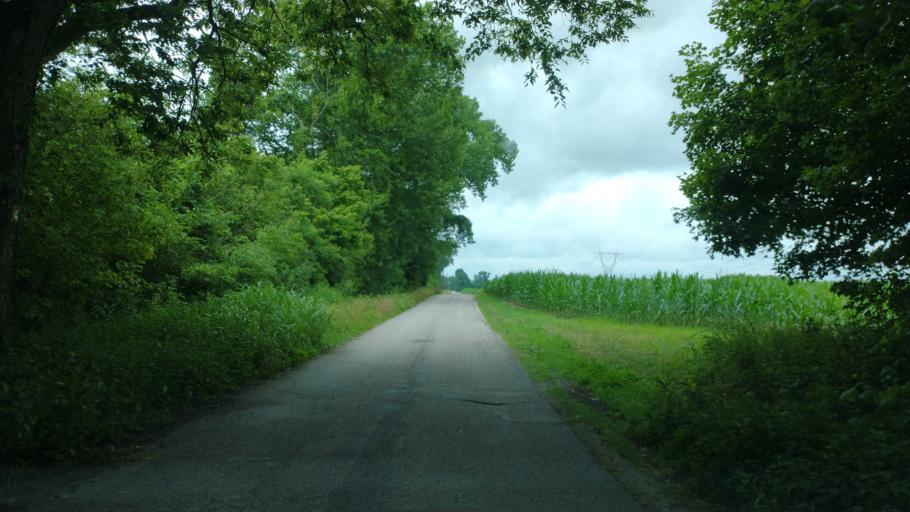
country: US
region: Ohio
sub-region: Meigs County
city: Middleport
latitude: 38.9342
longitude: -82.0833
